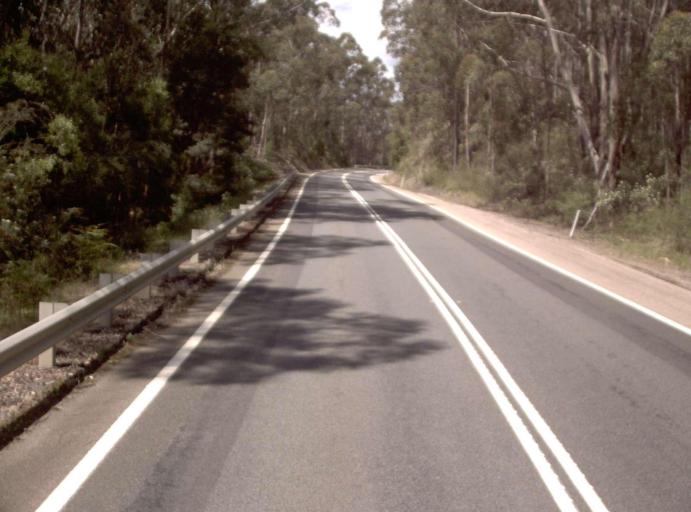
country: AU
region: New South Wales
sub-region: Bombala
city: Bombala
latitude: -37.5664
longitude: 149.3379
